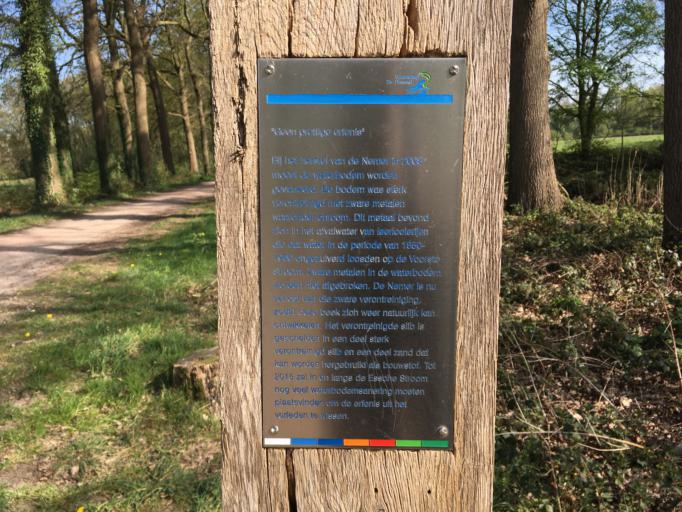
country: NL
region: North Brabant
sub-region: Gemeente Haaren
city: Haaren
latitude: 51.5891
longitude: 5.2348
